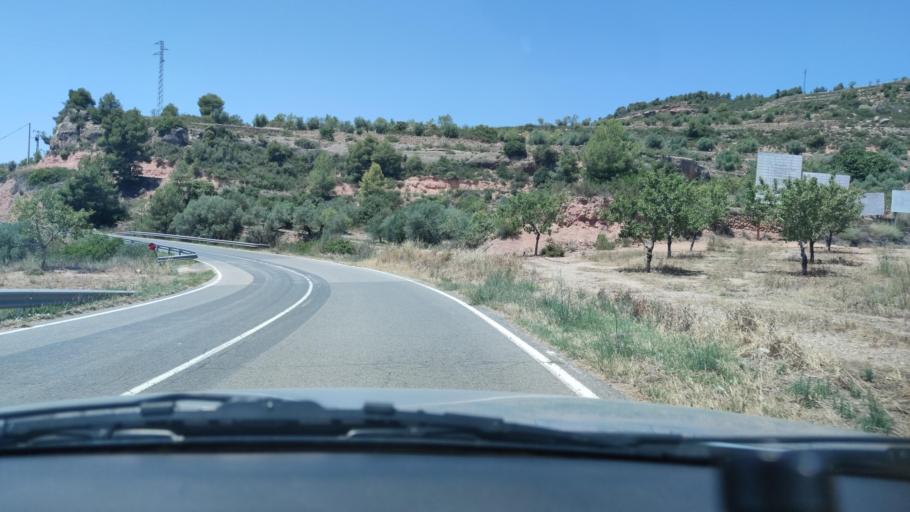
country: ES
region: Catalonia
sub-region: Provincia de Lleida
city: Juncosa
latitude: 41.3773
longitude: 0.7677
